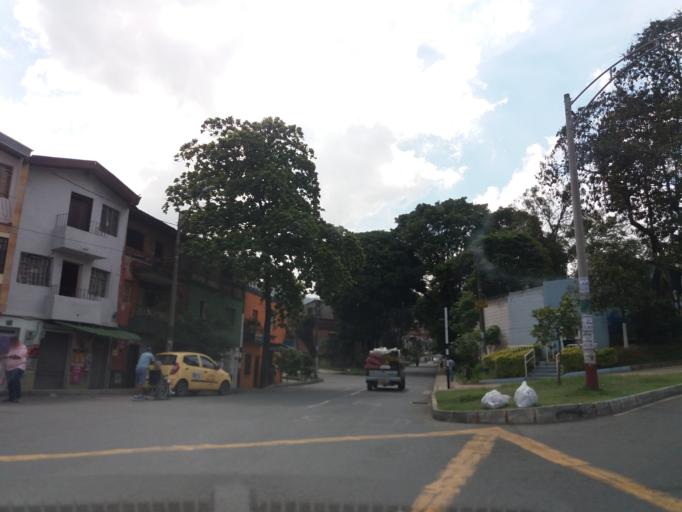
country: CO
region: Antioquia
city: Medellin
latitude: 6.2852
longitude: -75.5629
